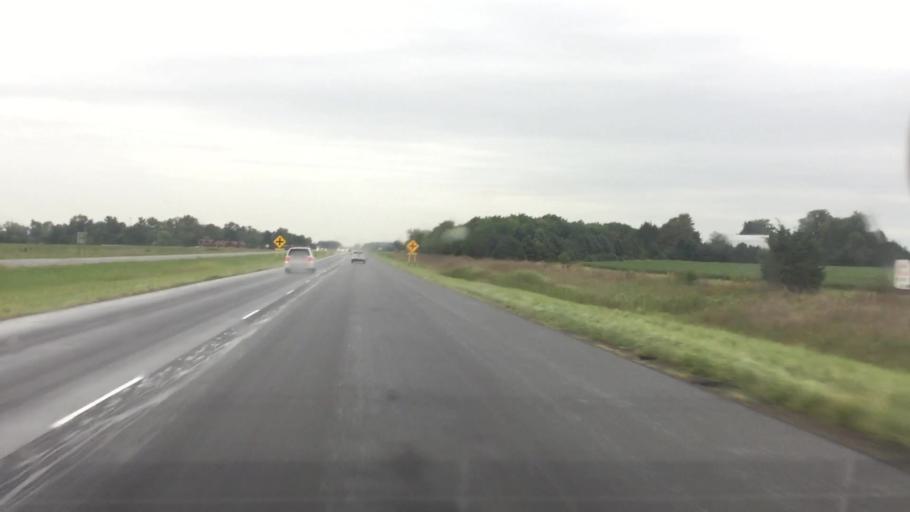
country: US
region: Ohio
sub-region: Henry County
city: Napoleon
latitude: 41.3774
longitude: -84.1809
